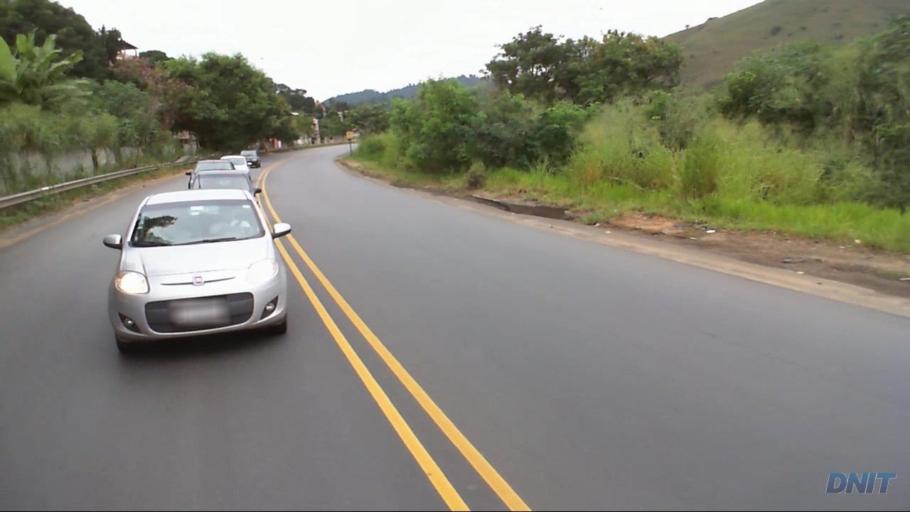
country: BR
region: Minas Gerais
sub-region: Coronel Fabriciano
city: Coronel Fabriciano
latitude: -19.5320
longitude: -42.6004
